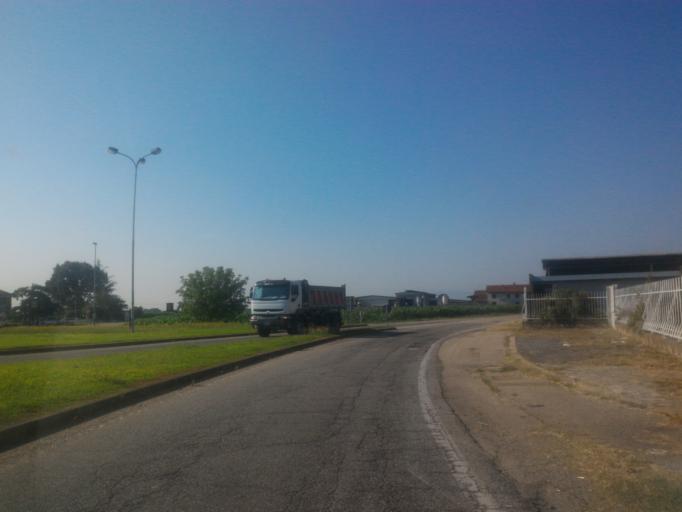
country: IT
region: Piedmont
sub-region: Provincia di Torino
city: Buriasco
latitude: 44.8690
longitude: 7.4141
